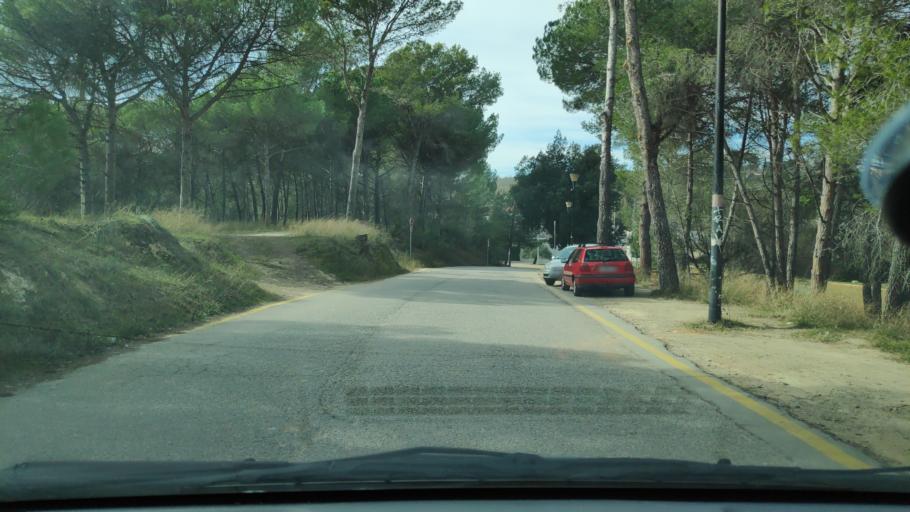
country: ES
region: Catalonia
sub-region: Provincia de Barcelona
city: Sant Quirze del Valles
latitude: 41.5003
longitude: 2.0924
